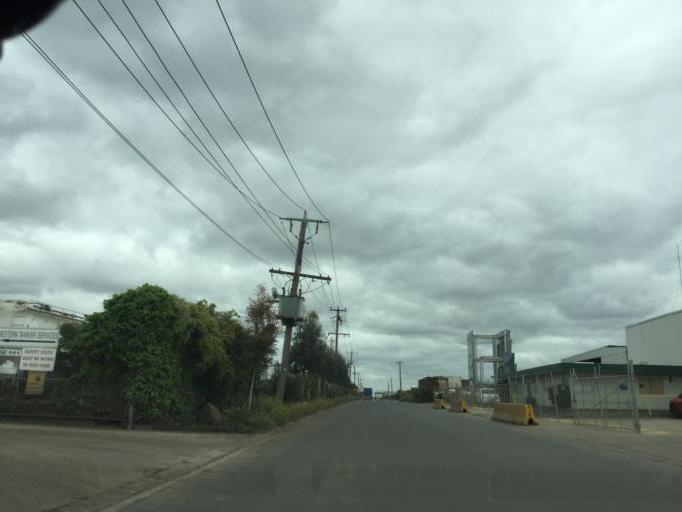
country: AU
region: Victoria
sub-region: Brimbank
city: Brooklyn
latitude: -37.8119
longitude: 144.8472
